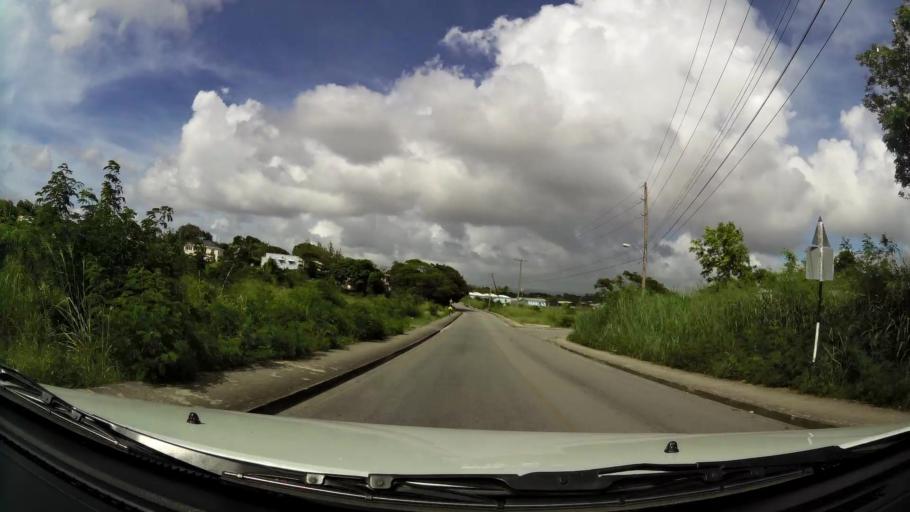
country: BB
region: Saint Michael
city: Bridgetown
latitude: 13.0966
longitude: -59.5931
